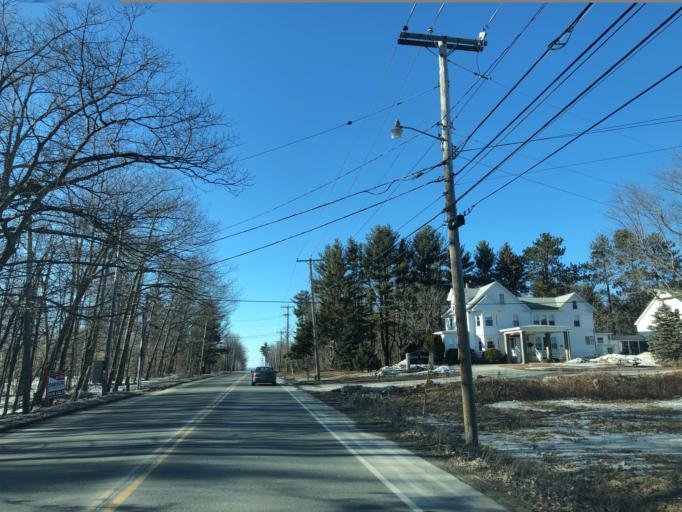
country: US
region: Maine
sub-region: Penobscot County
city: Bangor
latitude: 44.8293
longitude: -68.7849
